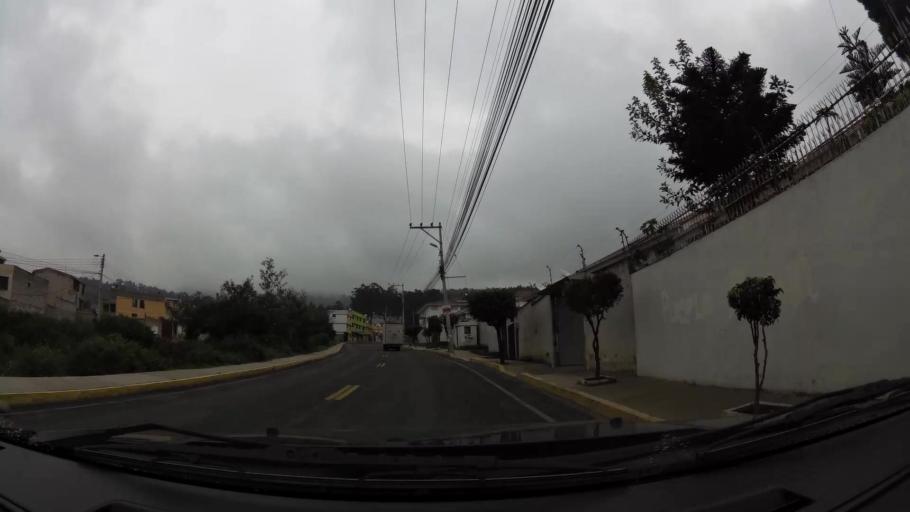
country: EC
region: Pichincha
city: Quito
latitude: -0.2649
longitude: -78.4743
